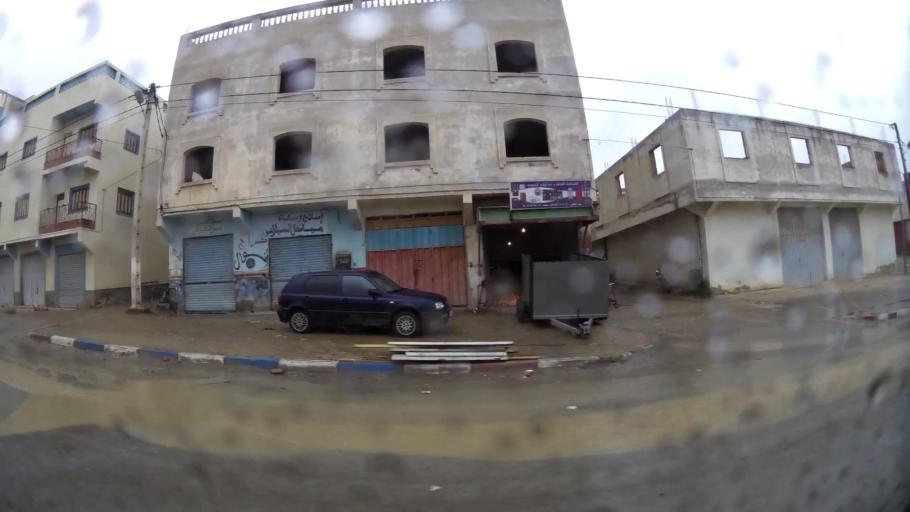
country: MA
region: Oriental
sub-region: Nador
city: Midar
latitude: 34.8830
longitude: -3.7267
